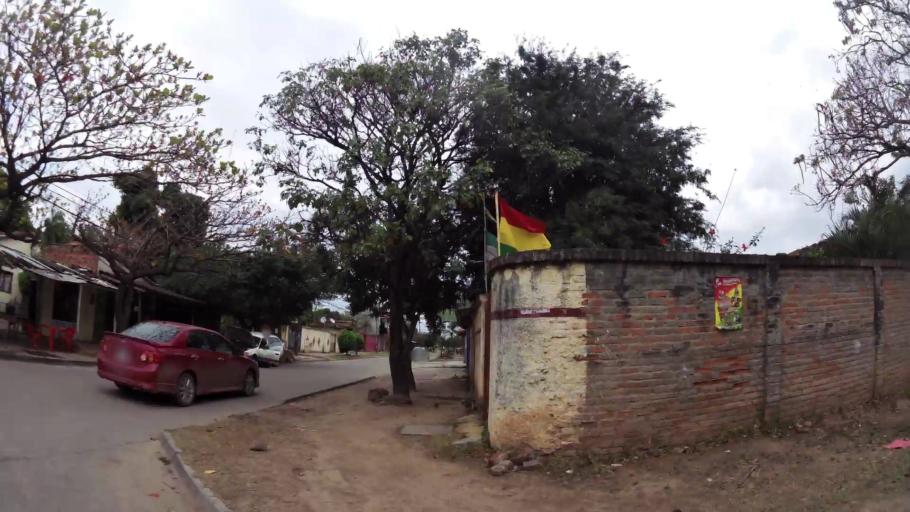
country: BO
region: Santa Cruz
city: Santa Cruz de la Sierra
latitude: -17.7437
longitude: -63.1898
